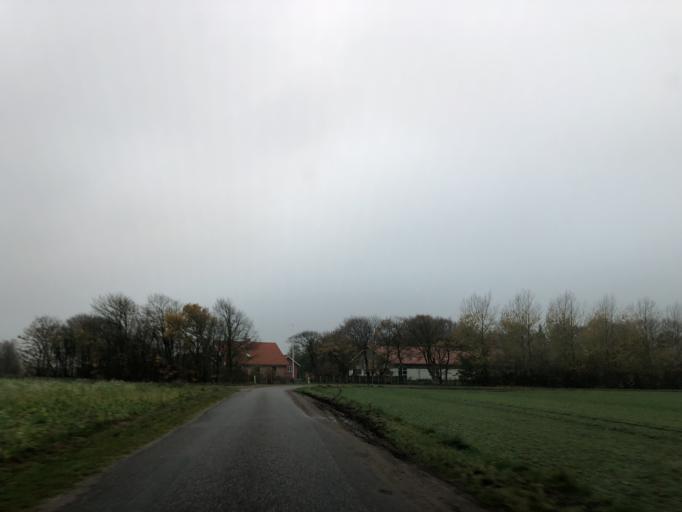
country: DK
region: Central Jutland
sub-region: Ringkobing-Skjern Kommune
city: Videbaek
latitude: 56.1966
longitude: 8.6536
